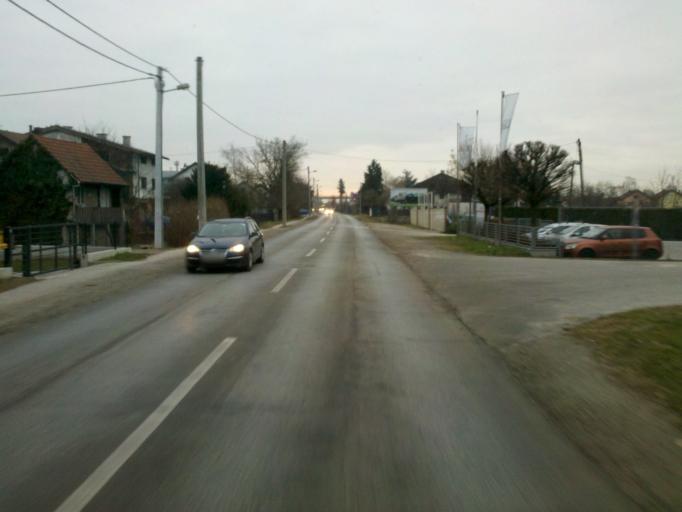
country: HR
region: Grad Zagreb
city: Lucko
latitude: 45.7605
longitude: 15.8878
